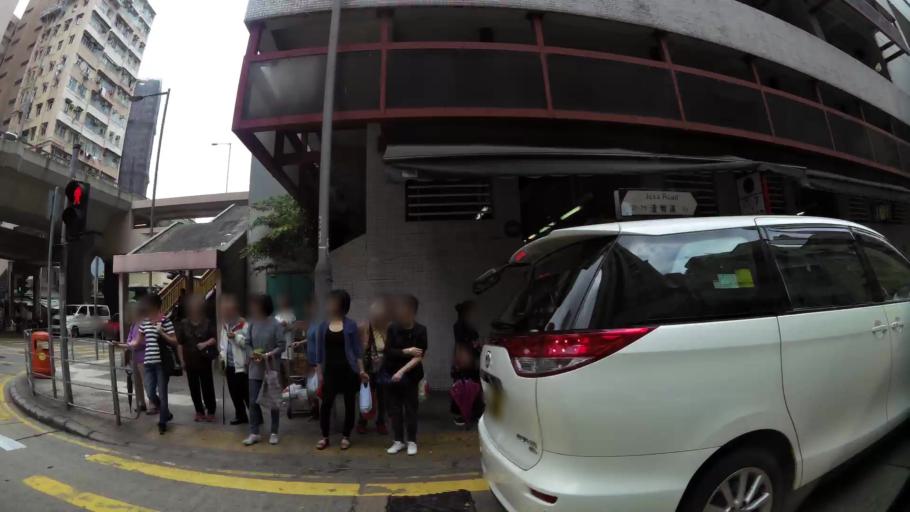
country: HK
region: Wanchai
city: Wan Chai
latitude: 22.2919
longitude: 114.1988
